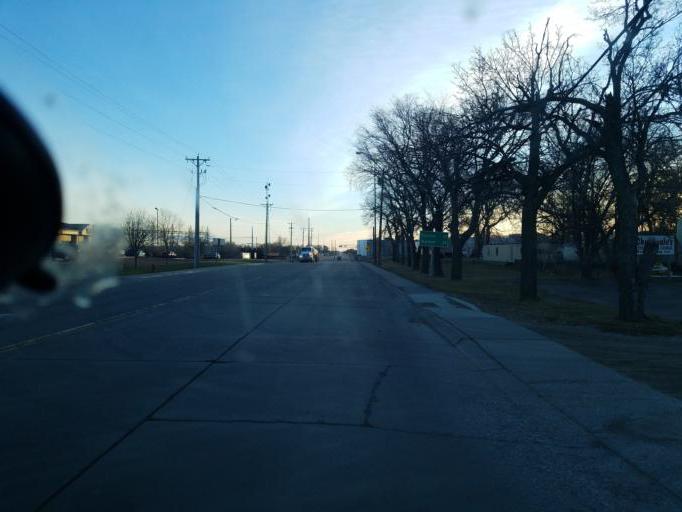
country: US
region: South Dakota
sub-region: Davison County
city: Mitchell
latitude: 43.7022
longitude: -98.0171
